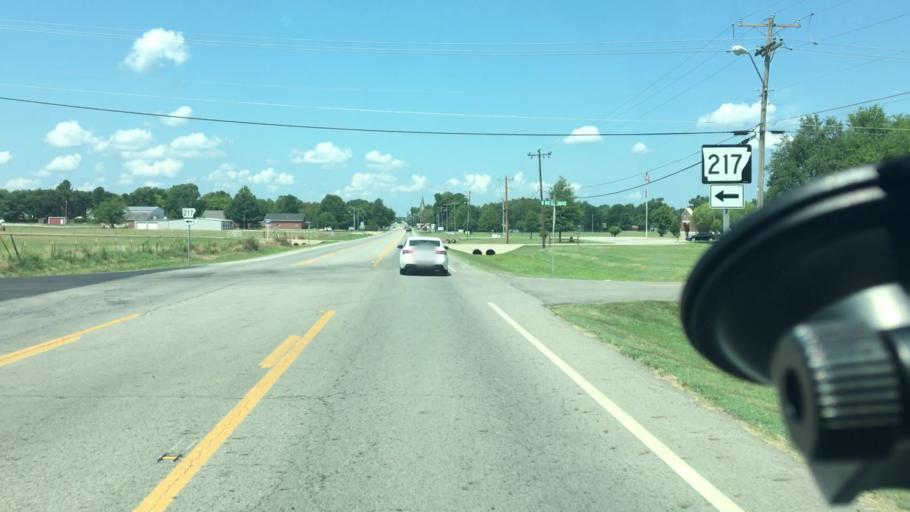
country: US
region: Arkansas
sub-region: Franklin County
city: Charleston
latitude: 35.2970
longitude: -94.0256
